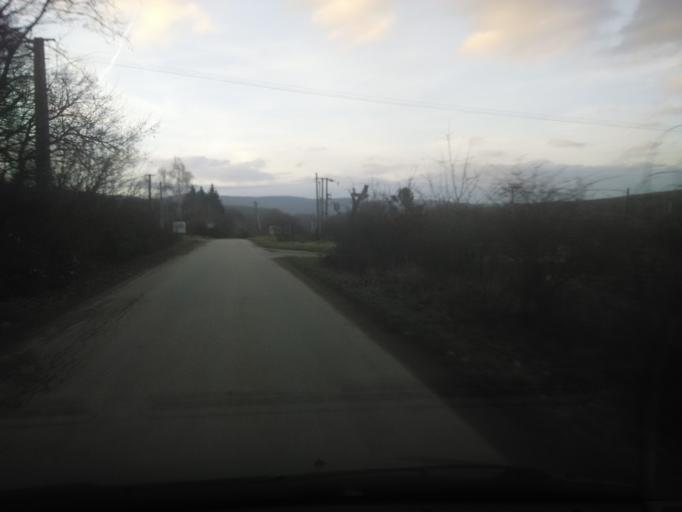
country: SK
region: Nitriansky
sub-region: Okres Nitra
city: Nitra
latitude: 48.3917
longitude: 18.2107
